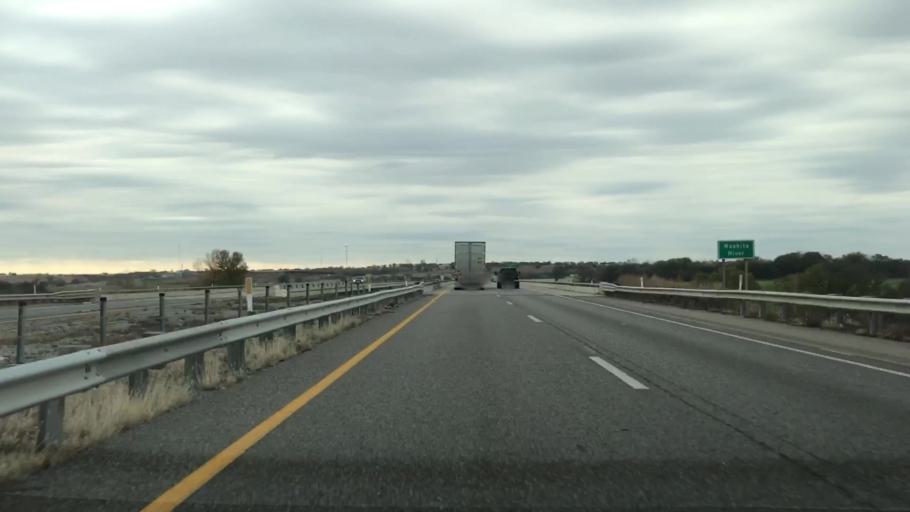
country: US
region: Oklahoma
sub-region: Custer County
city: Clinton
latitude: 35.5037
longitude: -98.9409
